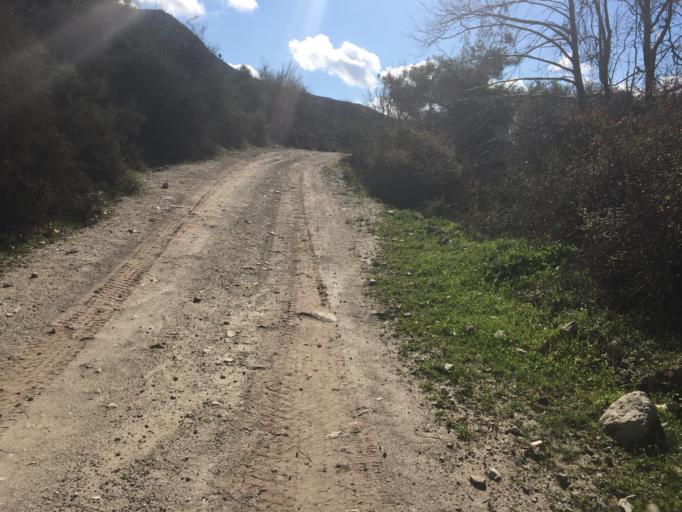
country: CY
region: Limassol
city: Pachna
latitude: 34.8805
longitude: 32.6776
